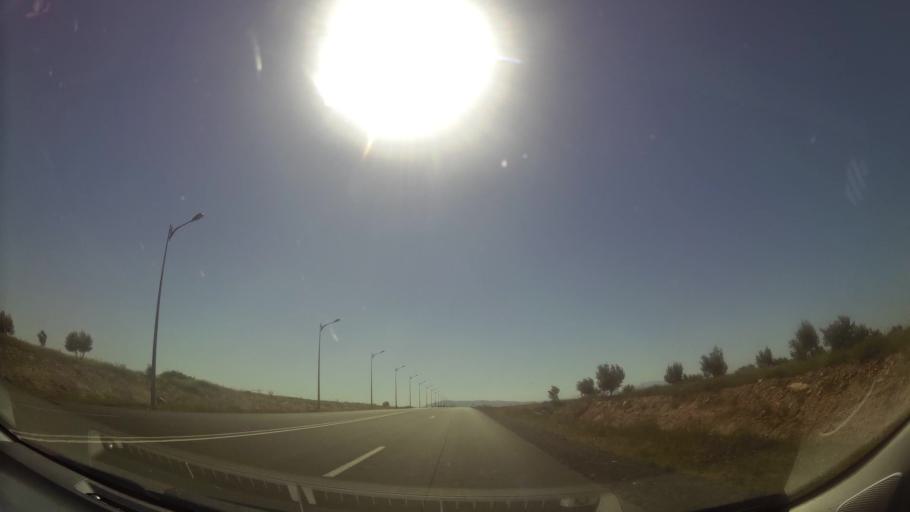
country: MA
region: Oriental
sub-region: Oujda-Angad
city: Oujda
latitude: 34.7408
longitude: -1.9035
